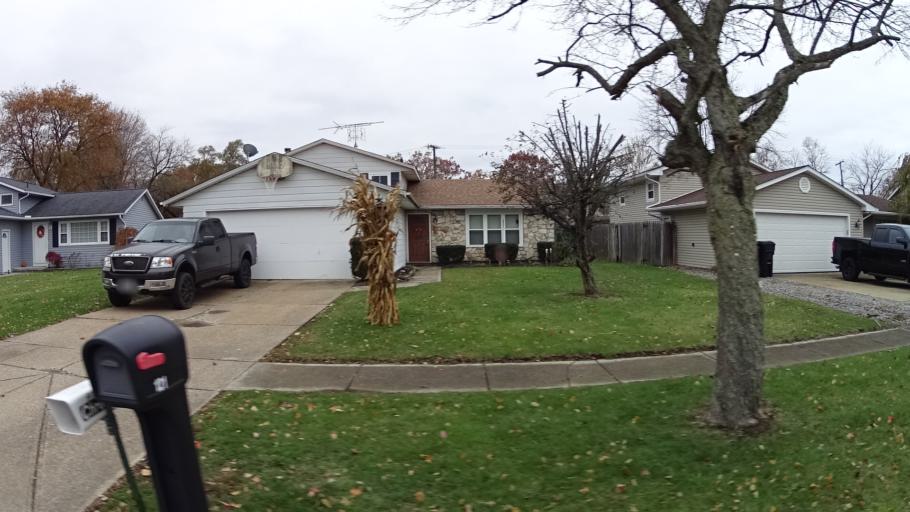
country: US
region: Ohio
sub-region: Lorain County
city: Sheffield
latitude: 41.4138
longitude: -82.0886
